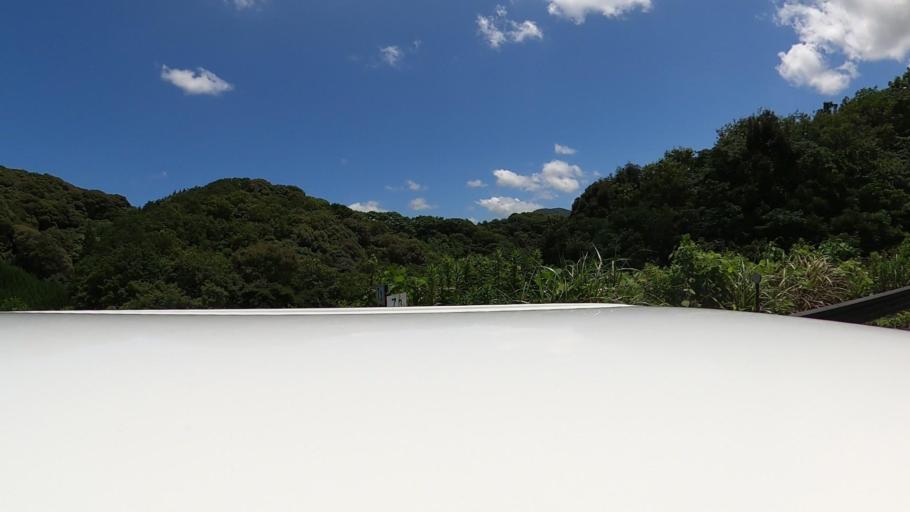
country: JP
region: Miyazaki
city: Nobeoka
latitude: 32.5714
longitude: 131.5636
